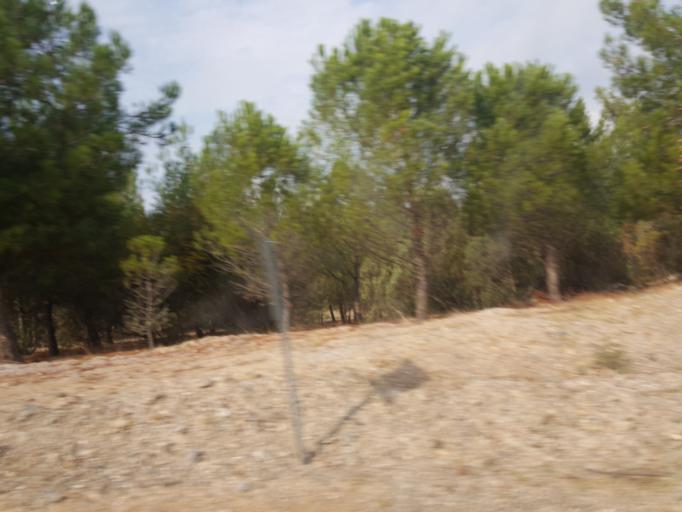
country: TR
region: Corum
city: Kamil
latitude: 41.1088
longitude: 34.7399
